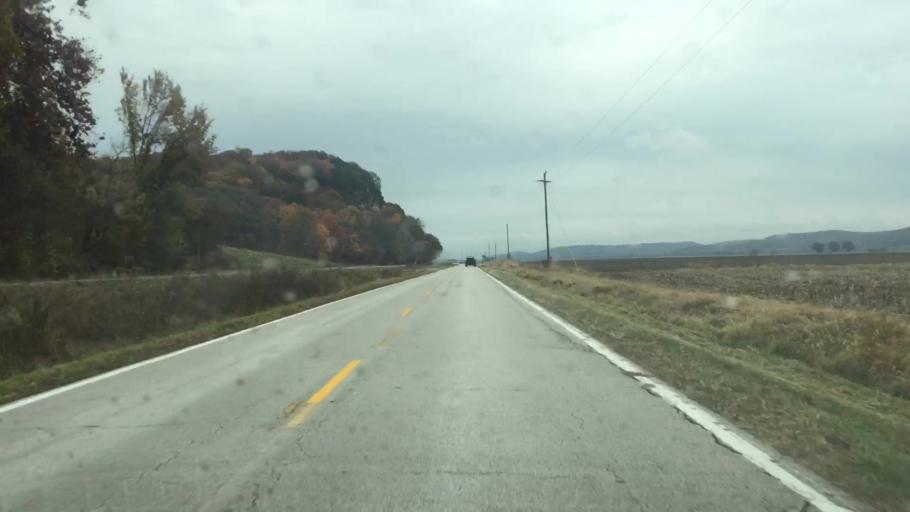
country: US
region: Missouri
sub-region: Gasconade County
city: Hermann
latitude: 38.7027
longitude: -91.5780
